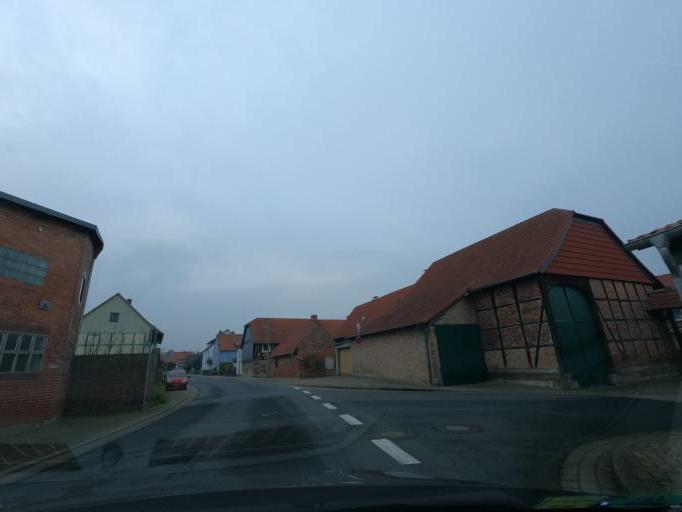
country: DE
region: Lower Saxony
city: Wolfenbuettel
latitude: 52.1973
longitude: 10.5820
